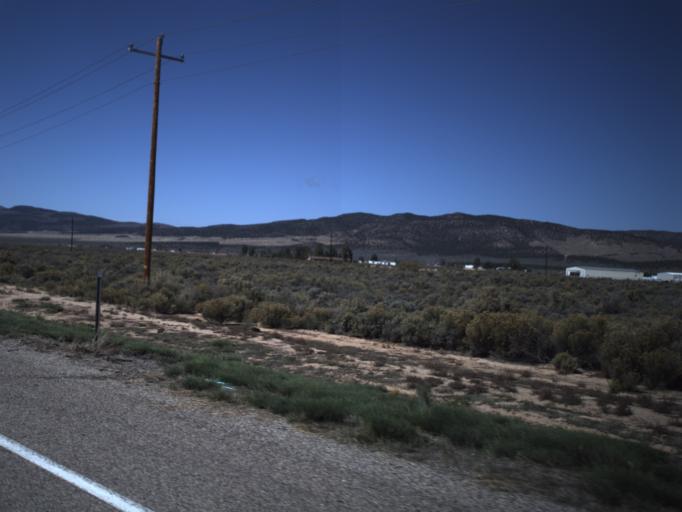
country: US
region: Utah
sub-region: Iron County
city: Cedar City
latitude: 37.6845
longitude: -113.1630
